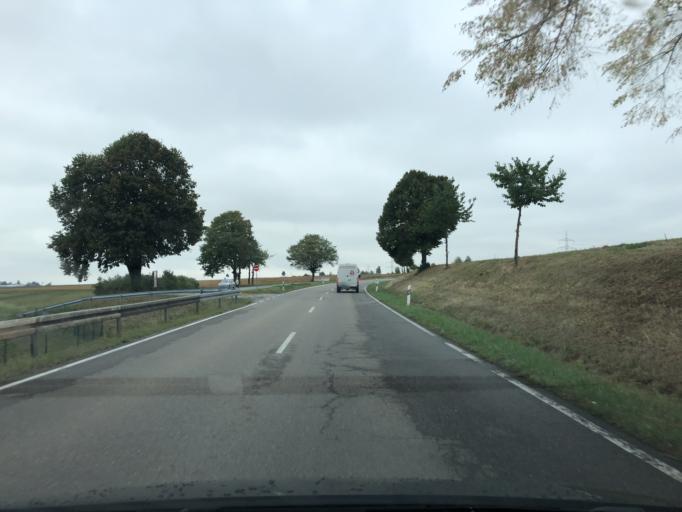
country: DE
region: Baden-Wuerttemberg
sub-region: Regierungsbezirk Stuttgart
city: Bondorf
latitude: 48.5025
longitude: 8.8174
